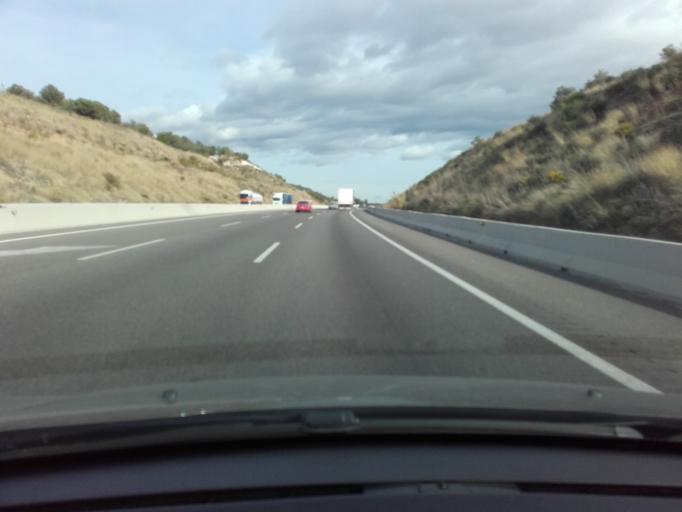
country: ES
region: Catalonia
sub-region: Provincia de Tarragona
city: els Pallaresos
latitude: 41.1439
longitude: 1.2865
